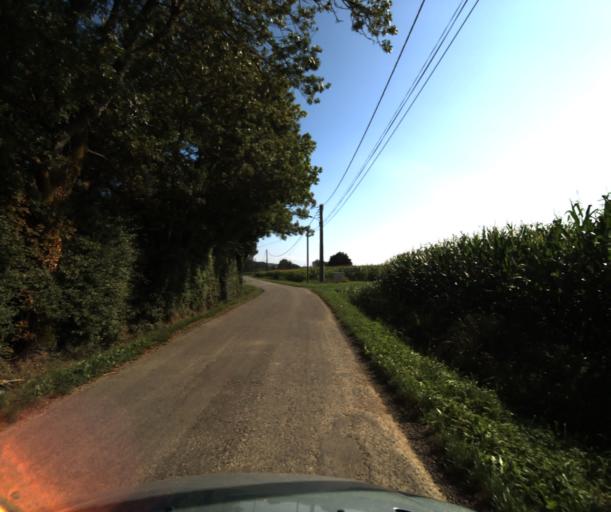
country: FR
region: Midi-Pyrenees
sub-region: Departement de la Haute-Garonne
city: Le Fauga
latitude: 43.4124
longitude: 1.3049
